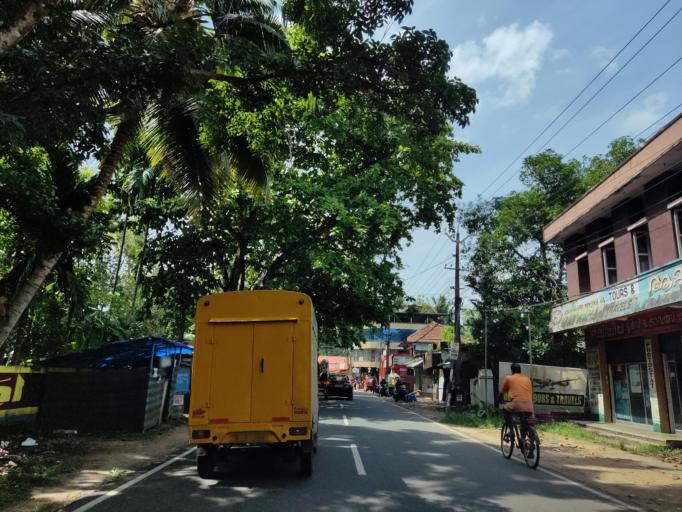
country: IN
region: Kerala
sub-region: Alappuzha
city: Mavelikara
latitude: 9.2763
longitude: 76.5365
